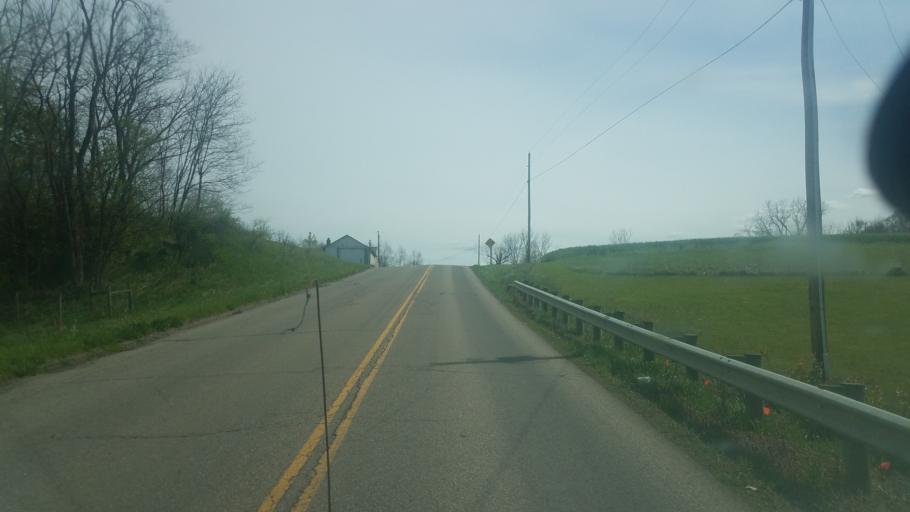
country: US
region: Ohio
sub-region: Holmes County
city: Millersburg
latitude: 40.5973
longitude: -81.8202
